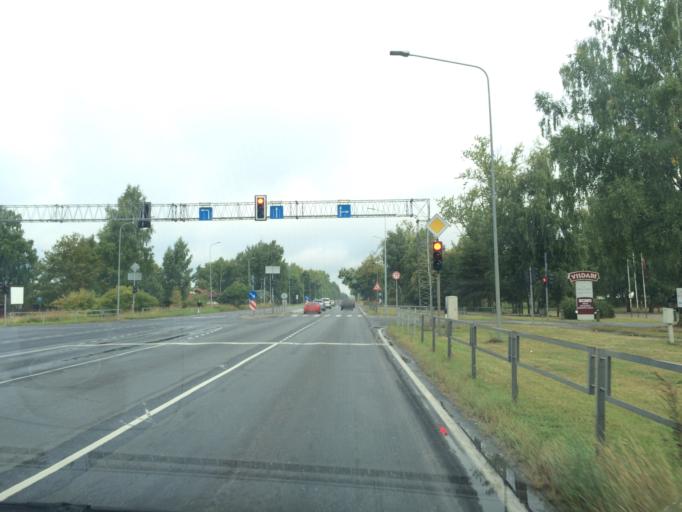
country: LV
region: Kekava
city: Kekava
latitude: 56.8700
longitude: 24.2749
